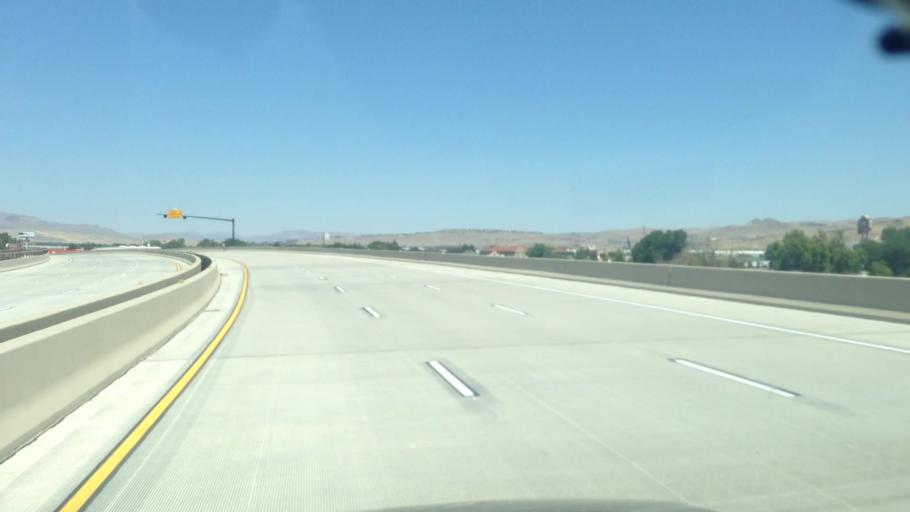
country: US
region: Nevada
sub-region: Washoe County
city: Sparks
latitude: 39.5179
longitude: -119.7112
